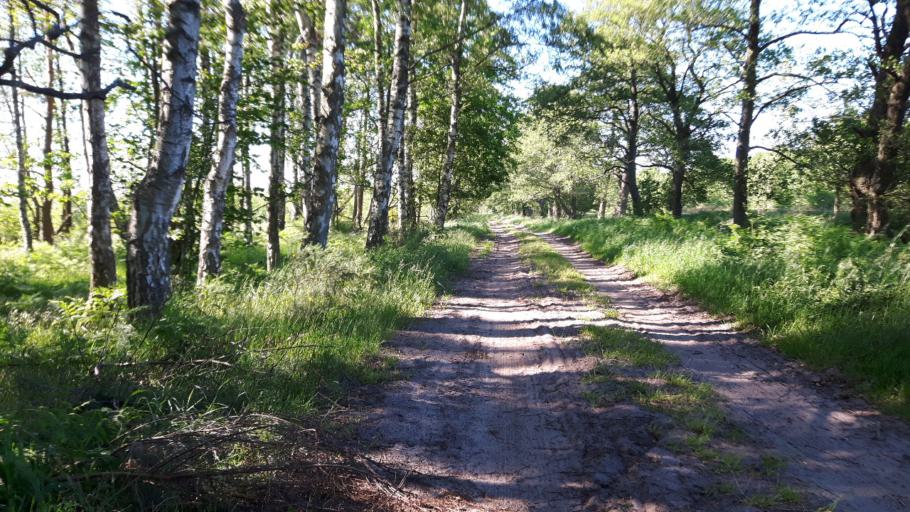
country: PL
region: Pomeranian Voivodeship
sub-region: Powiat leborski
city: Leba
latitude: 54.7157
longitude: 17.5263
